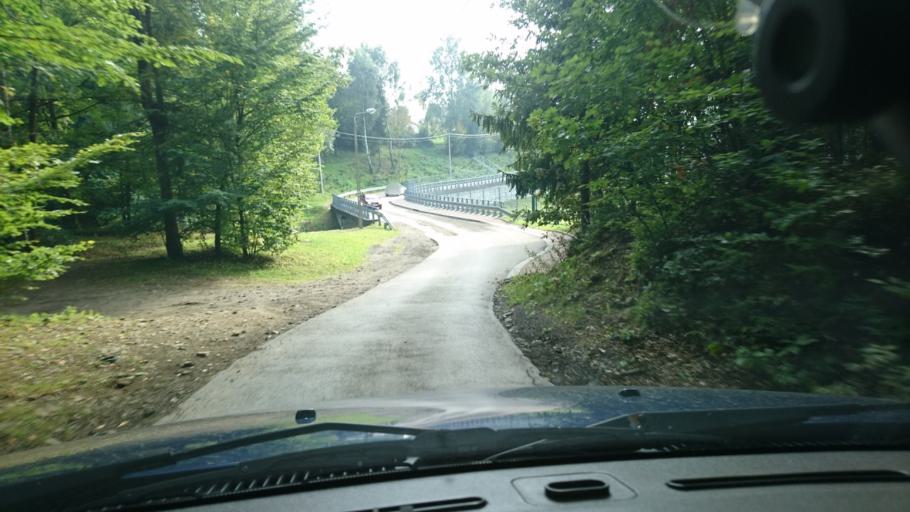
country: PL
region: Silesian Voivodeship
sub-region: Powiat bielski
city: Wilkowice
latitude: 49.7609
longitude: 19.1149
